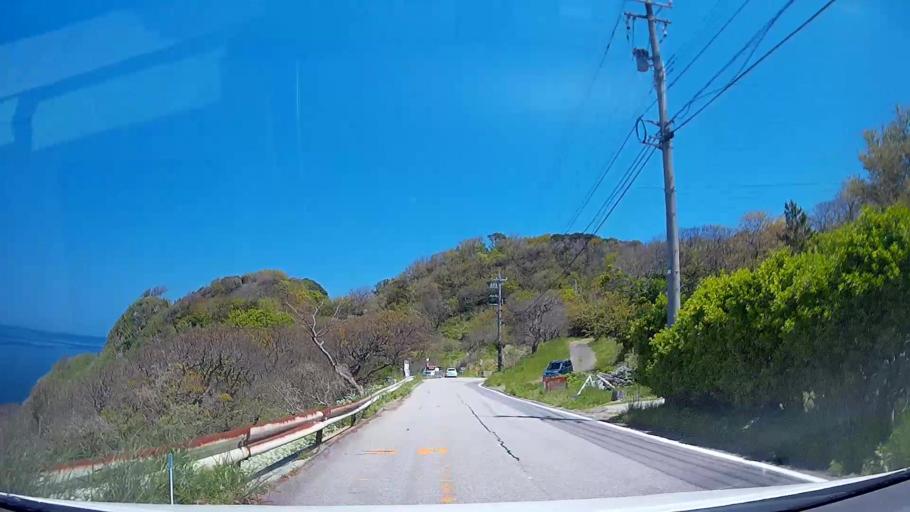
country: JP
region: Ishikawa
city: Nanao
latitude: 37.5298
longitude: 137.2730
